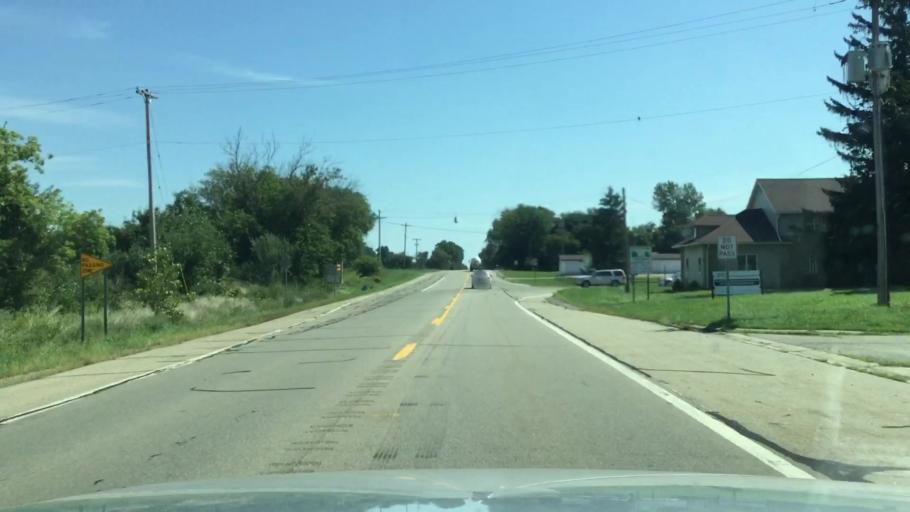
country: US
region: Michigan
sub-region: Washtenaw County
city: Manchester
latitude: 42.0725
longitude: -84.0677
